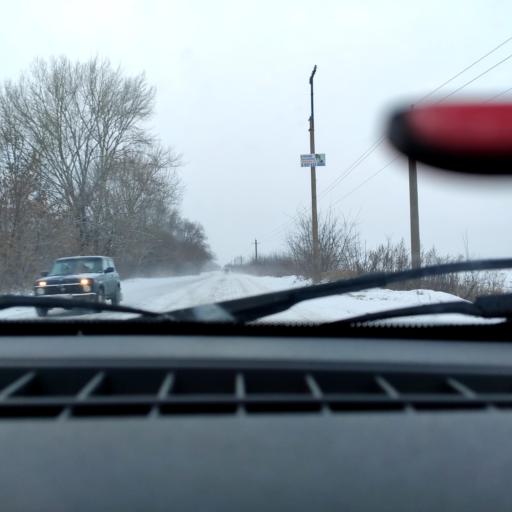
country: RU
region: Bashkortostan
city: Blagoveshchensk
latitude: 54.9130
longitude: 55.9932
